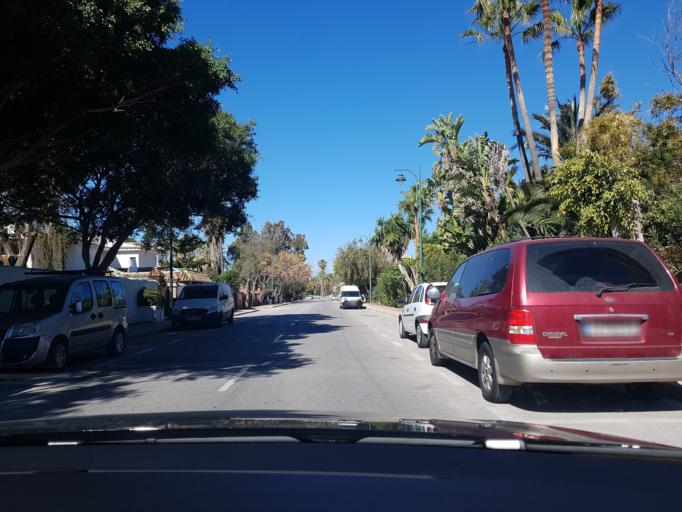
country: ES
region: Andalusia
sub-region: Provincia de Malaga
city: Torremolinos
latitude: 36.6668
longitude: -4.4585
